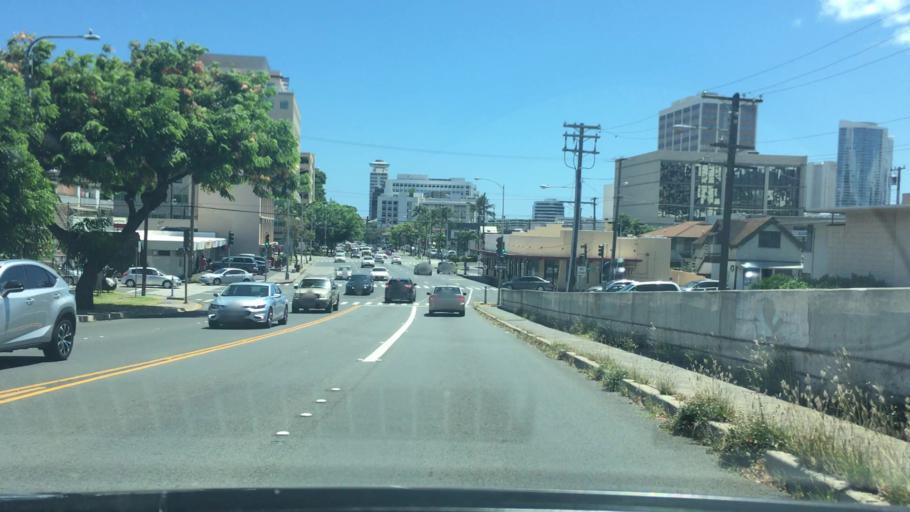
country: US
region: Hawaii
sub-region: Honolulu County
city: Honolulu
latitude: 21.3017
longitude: -157.8388
